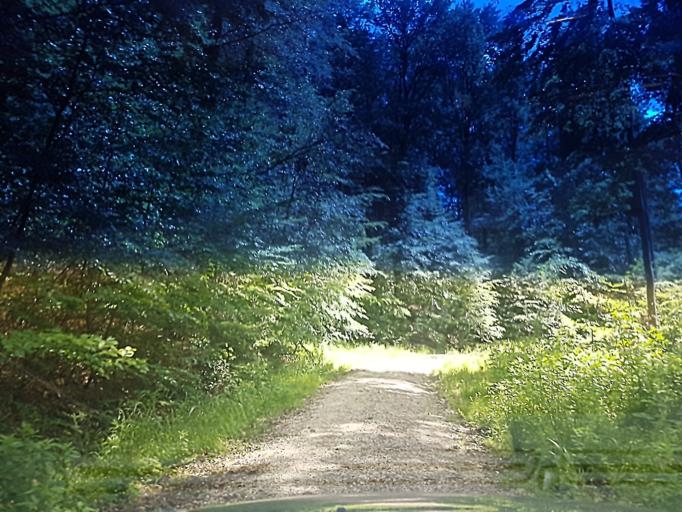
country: DE
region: Bavaria
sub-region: Upper Franconia
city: Litzendorf
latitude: 49.9382
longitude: 11.0254
